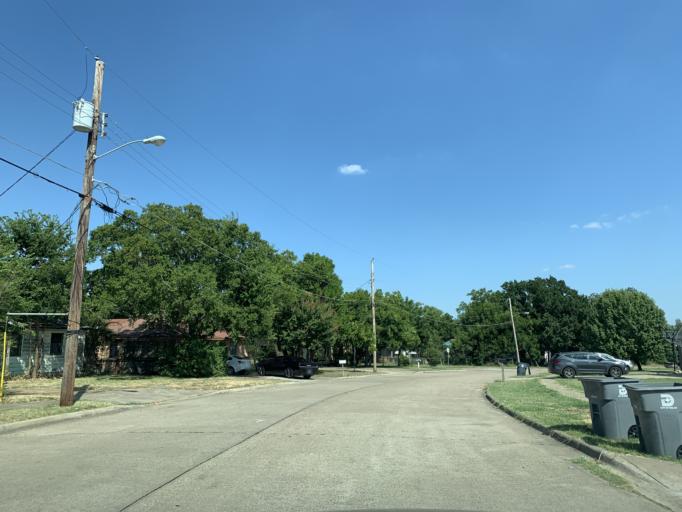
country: US
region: Texas
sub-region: Dallas County
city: Hutchins
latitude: 32.6563
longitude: -96.7735
